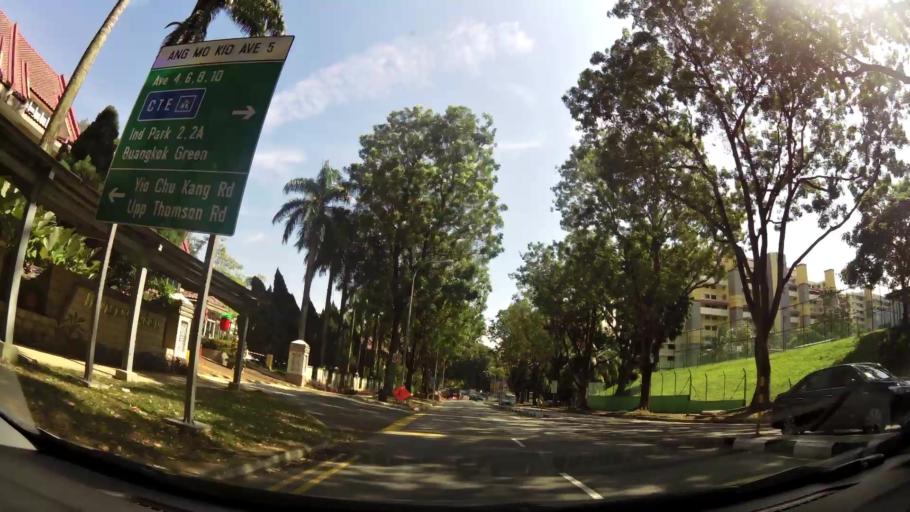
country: SG
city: Singapore
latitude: 1.3770
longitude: 103.8351
